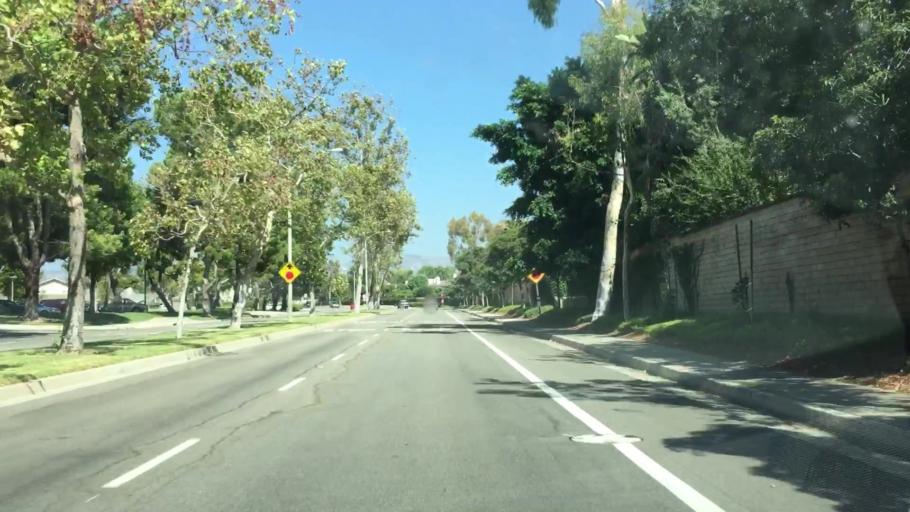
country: US
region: California
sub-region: Orange County
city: North Tustin
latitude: 33.7103
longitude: -117.7667
